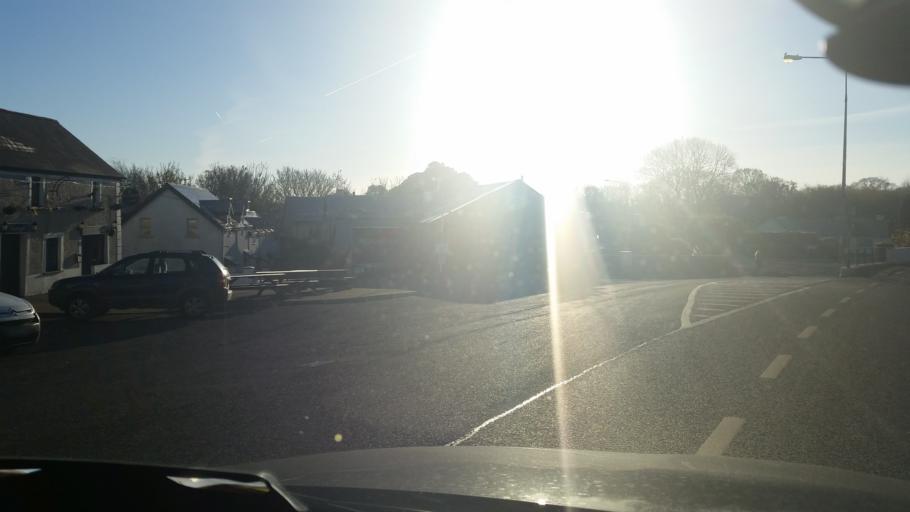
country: IE
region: Leinster
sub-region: Loch Garman
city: Gorey
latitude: 52.6096
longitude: -6.3044
